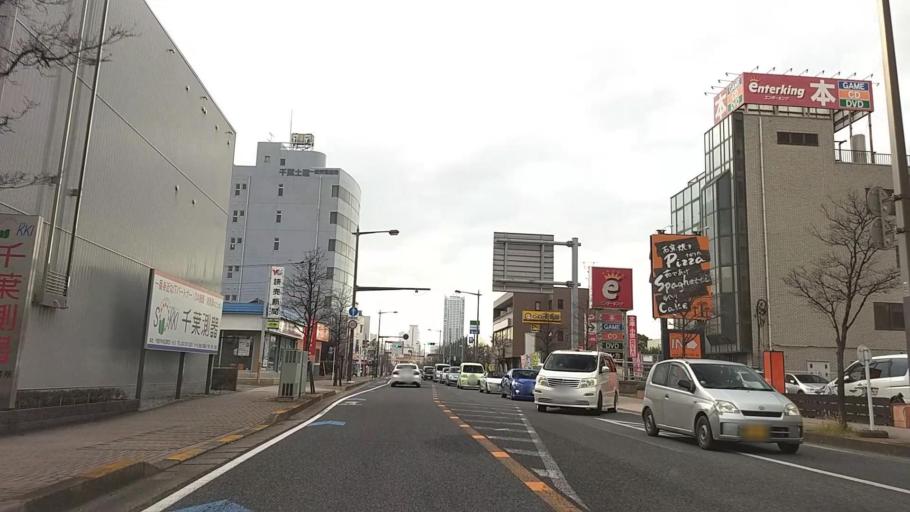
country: JP
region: Chiba
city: Chiba
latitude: 35.6093
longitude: 140.1362
